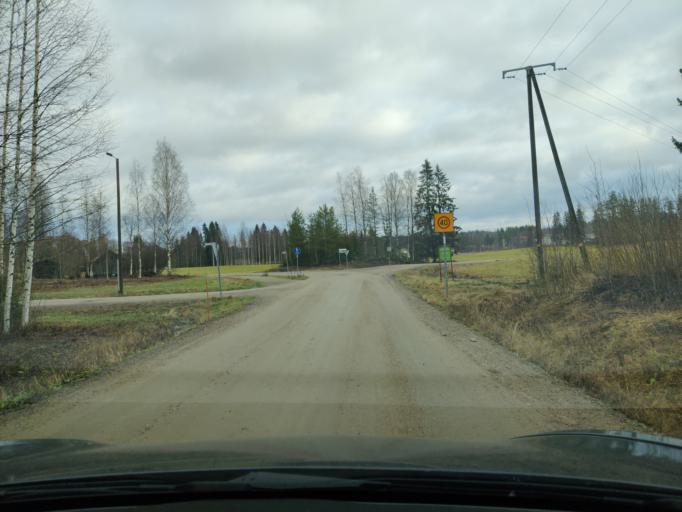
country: FI
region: Northern Savo
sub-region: Ylae-Savo
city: Kiuruvesi
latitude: 63.6389
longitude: 26.6405
